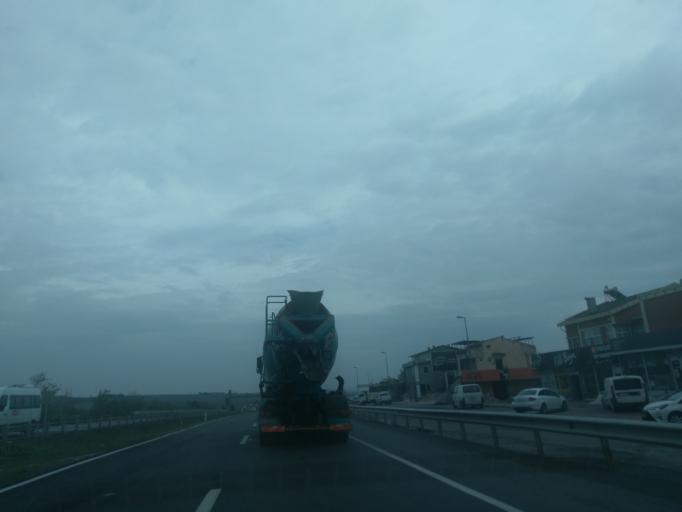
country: TR
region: Istanbul
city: Canta
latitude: 41.0760
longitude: 28.1427
